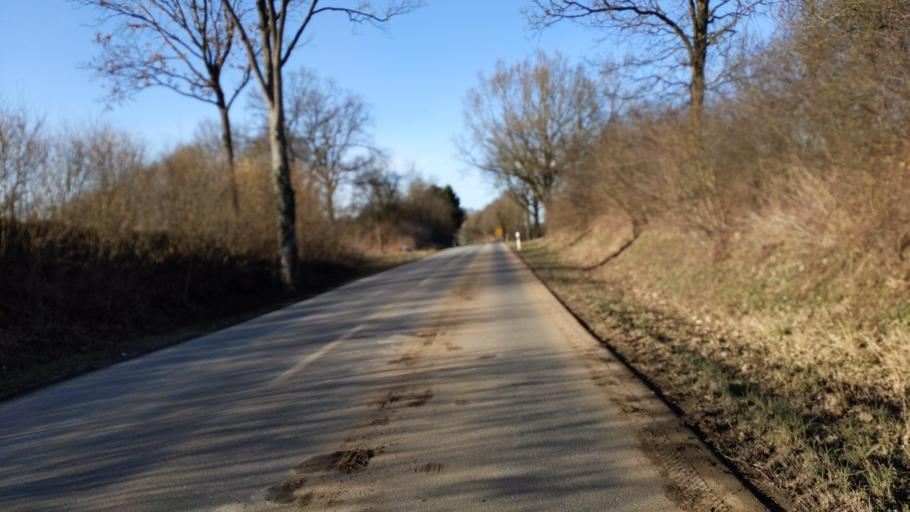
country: DE
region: Schleswig-Holstein
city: Susel
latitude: 54.0608
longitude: 10.6487
